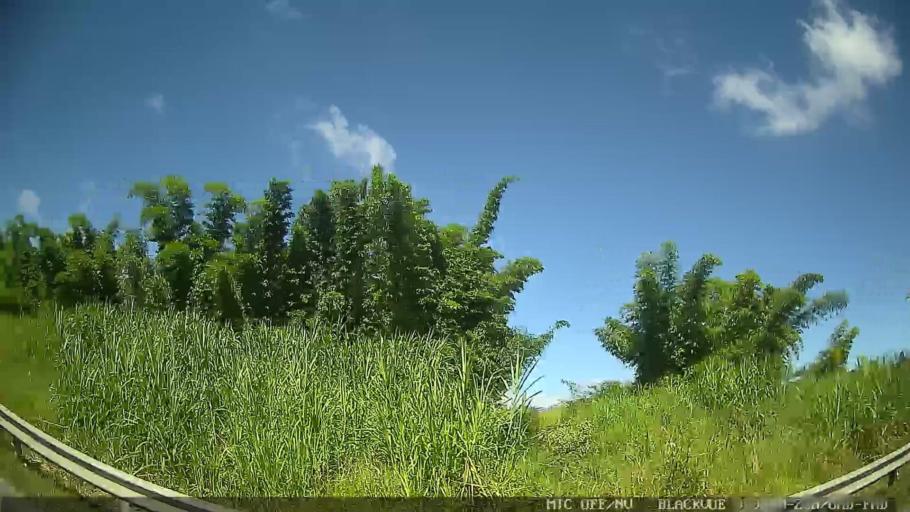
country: BR
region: Sao Paulo
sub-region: Suzano
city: Suzano
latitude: -23.5618
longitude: -46.2562
